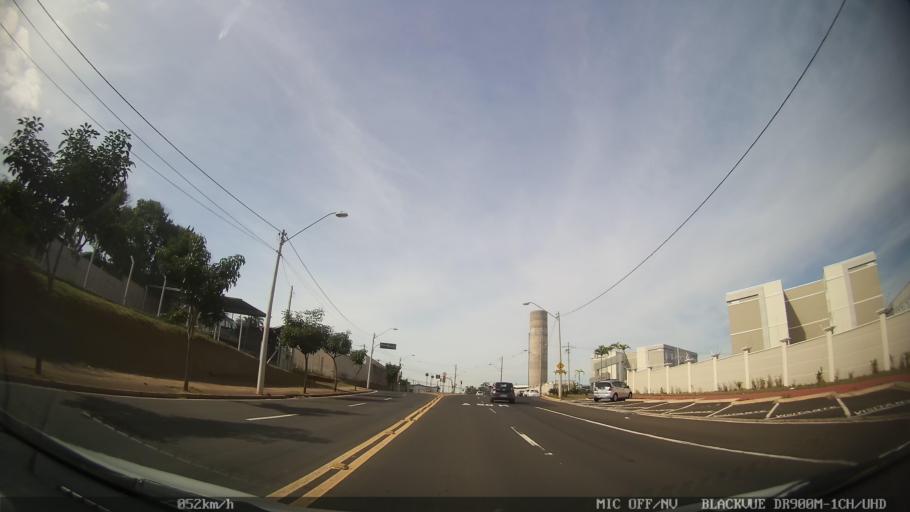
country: BR
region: Sao Paulo
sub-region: Piracicaba
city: Piracicaba
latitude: -22.7483
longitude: -47.6225
